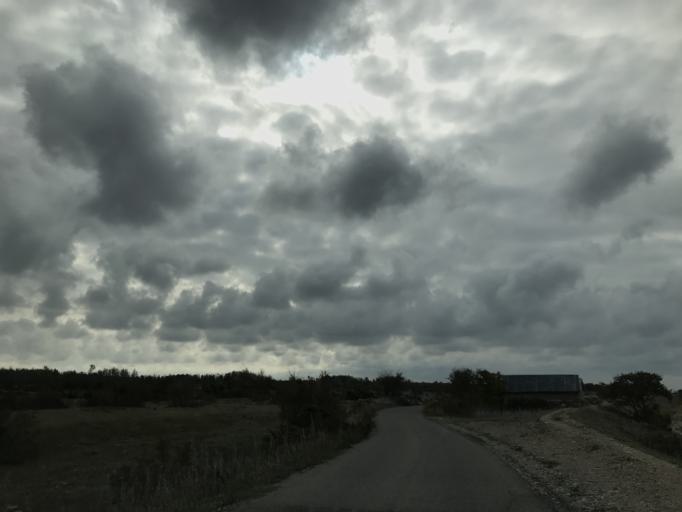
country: SE
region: Kalmar
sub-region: Borgholms Kommun
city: Borgholm
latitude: 57.0504
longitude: 16.8357
